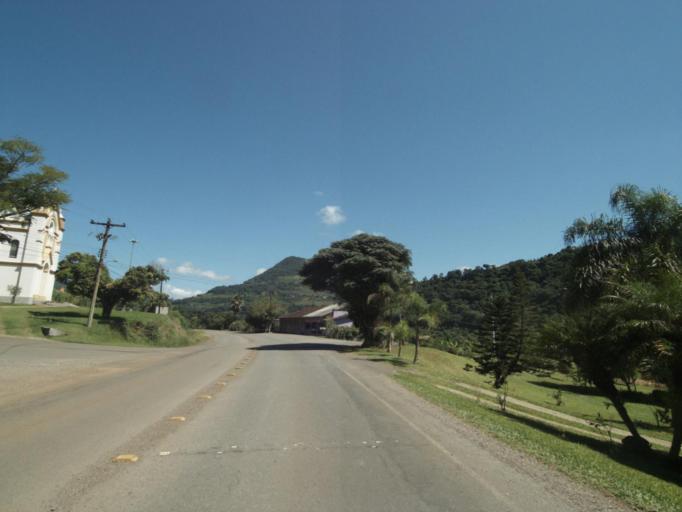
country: BR
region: Rio Grande do Sul
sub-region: Bento Goncalves
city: Bento Goncalves
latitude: -29.0934
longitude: -51.6278
